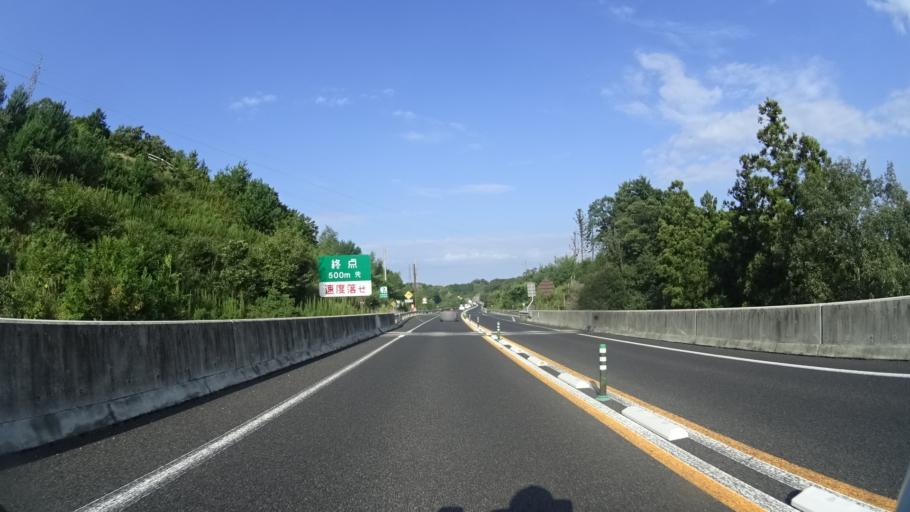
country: JP
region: Shimane
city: Izumo
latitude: 35.3253
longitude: 132.7247
